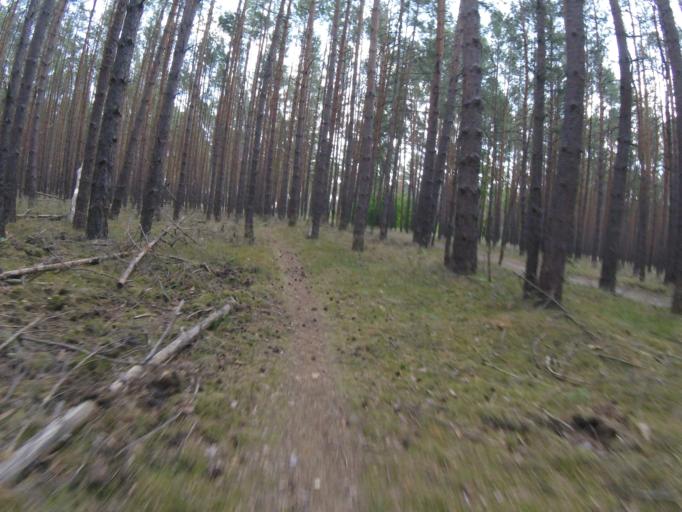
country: DE
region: Brandenburg
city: Bestensee
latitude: 52.2686
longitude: 13.6972
